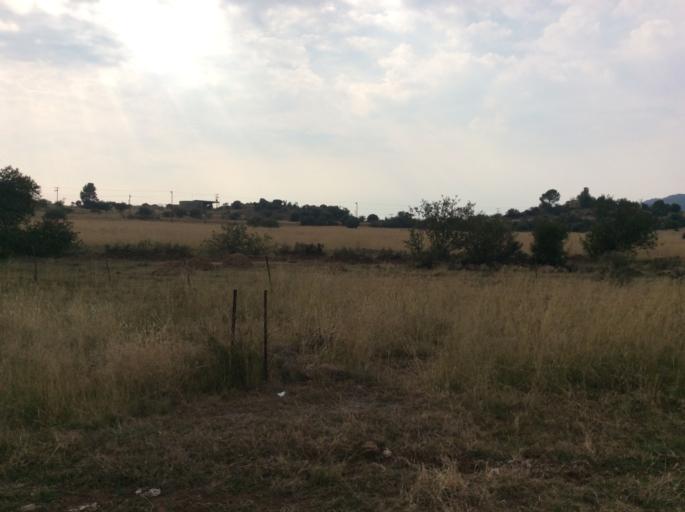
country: LS
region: Mafeteng
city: Mafeteng
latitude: -29.9881
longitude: 27.0193
